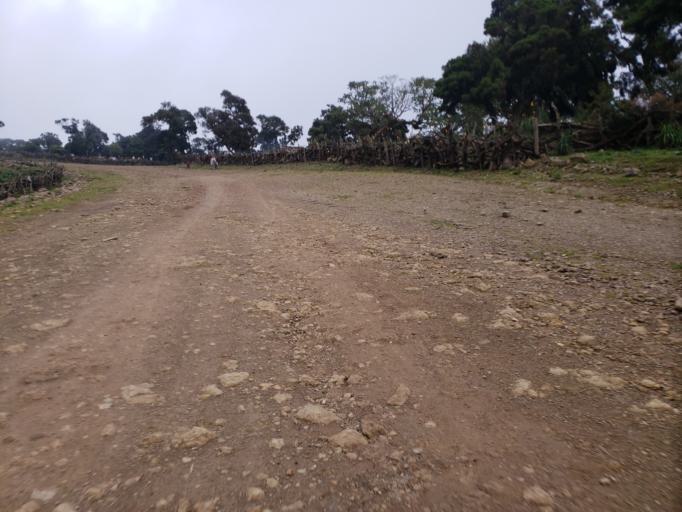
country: ET
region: Oromiya
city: Dodola
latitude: 6.7257
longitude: 39.4260
